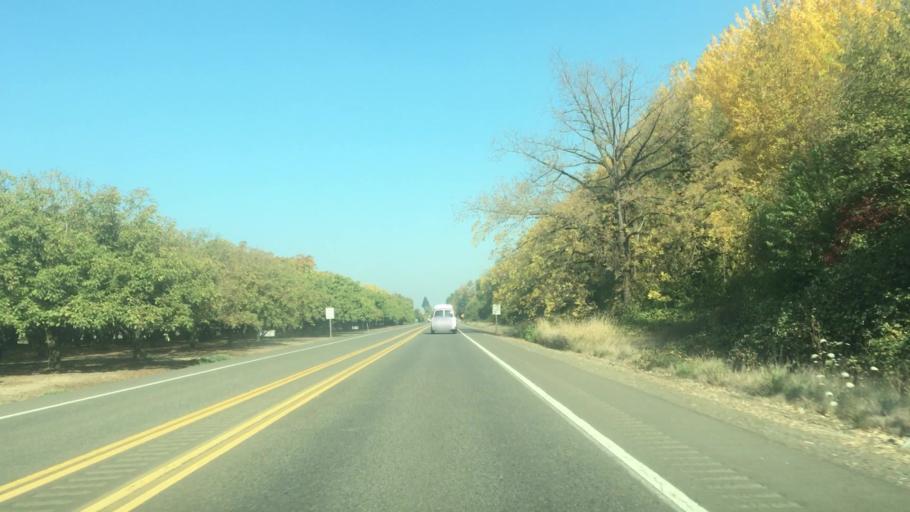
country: US
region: Oregon
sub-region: Yamhill County
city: Amity
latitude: 45.1620
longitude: -123.2579
